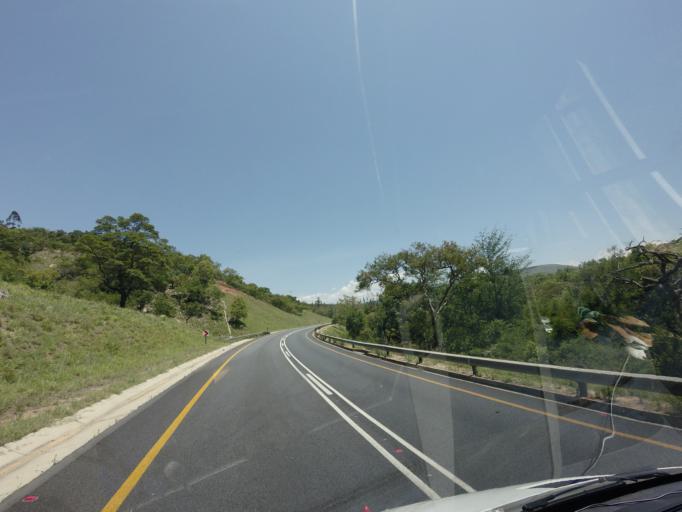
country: ZA
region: Mpumalanga
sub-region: Ehlanzeni District
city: Nelspruit
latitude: -25.4595
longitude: 30.6931
